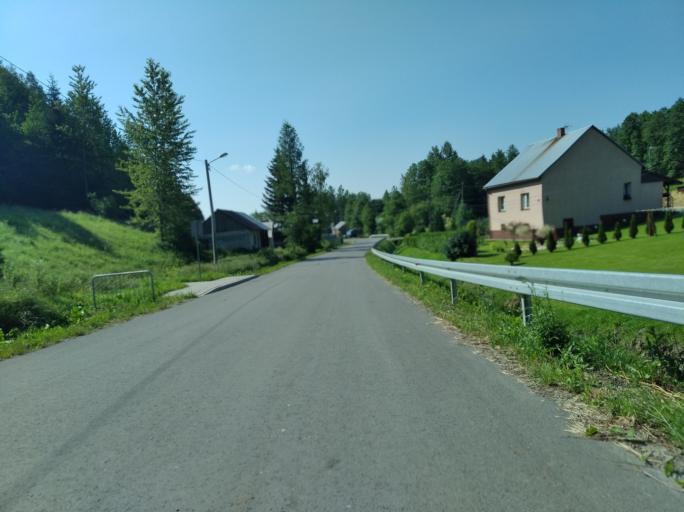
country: PL
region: Subcarpathian Voivodeship
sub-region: Powiat brzozowski
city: Nozdrzec
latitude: 49.8239
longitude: 22.1630
